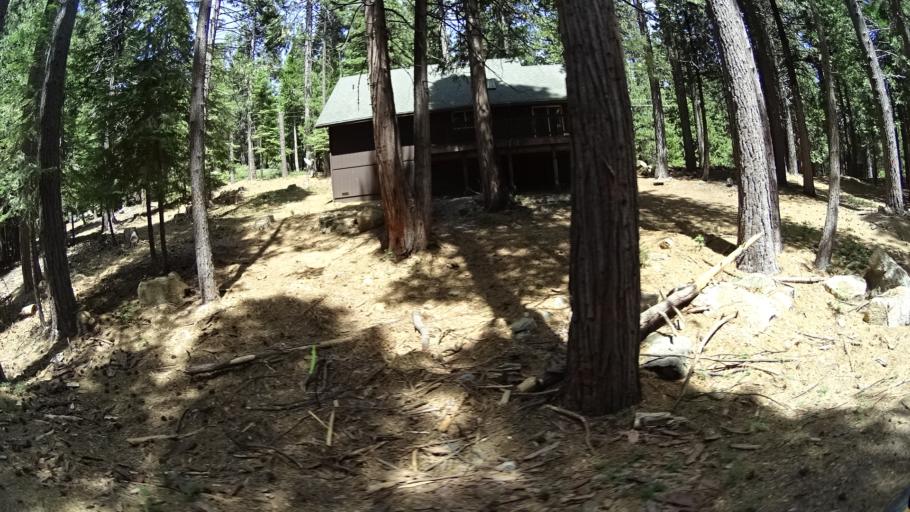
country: US
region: California
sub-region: Calaveras County
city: Arnold
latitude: 38.3042
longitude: -120.2657
